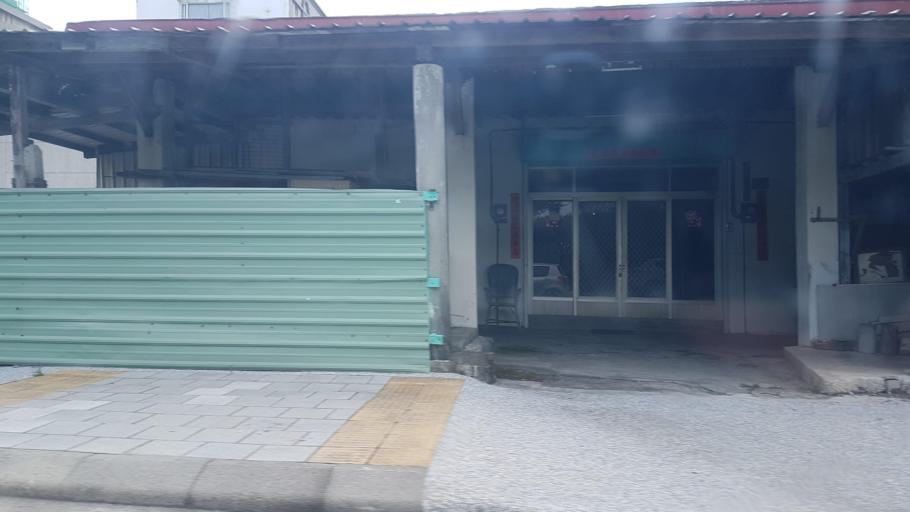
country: TW
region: Taiwan
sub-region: Hualien
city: Hualian
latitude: 23.9964
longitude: 121.6332
